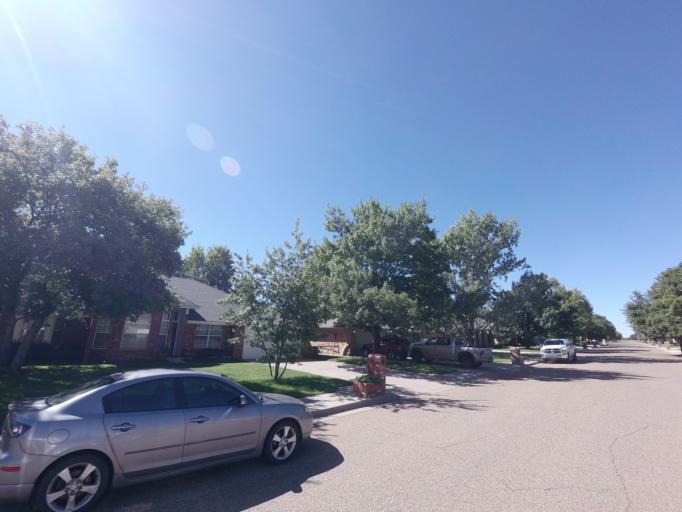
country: US
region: New Mexico
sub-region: Curry County
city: Clovis
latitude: 34.4215
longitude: -103.1726
